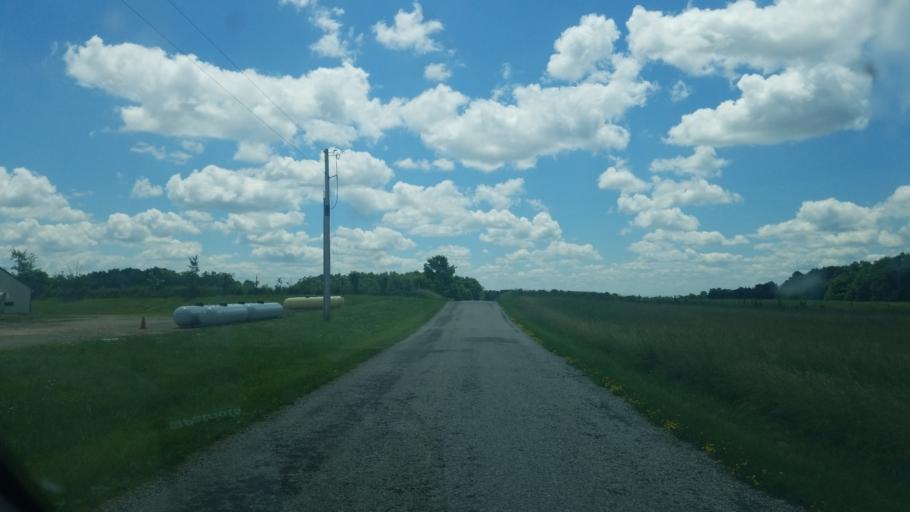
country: US
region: Ohio
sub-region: Huron County
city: New London
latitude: 40.9904
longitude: -82.3268
